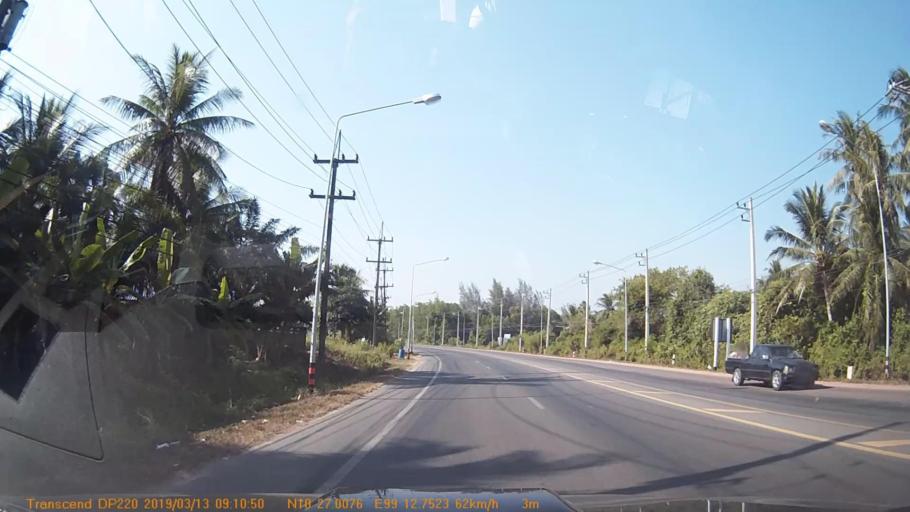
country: TH
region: Chumphon
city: Chumphon
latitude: 10.4498
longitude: 99.2124
